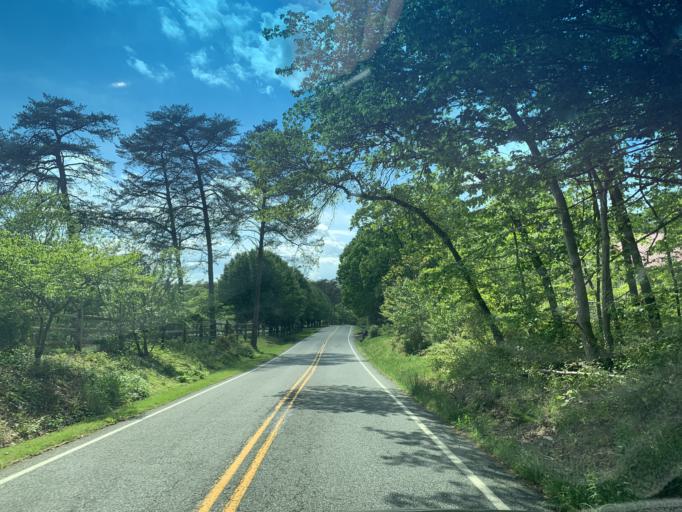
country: US
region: Maryland
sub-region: Cecil County
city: Rising Sun
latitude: 39.7208
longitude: -76.1735
